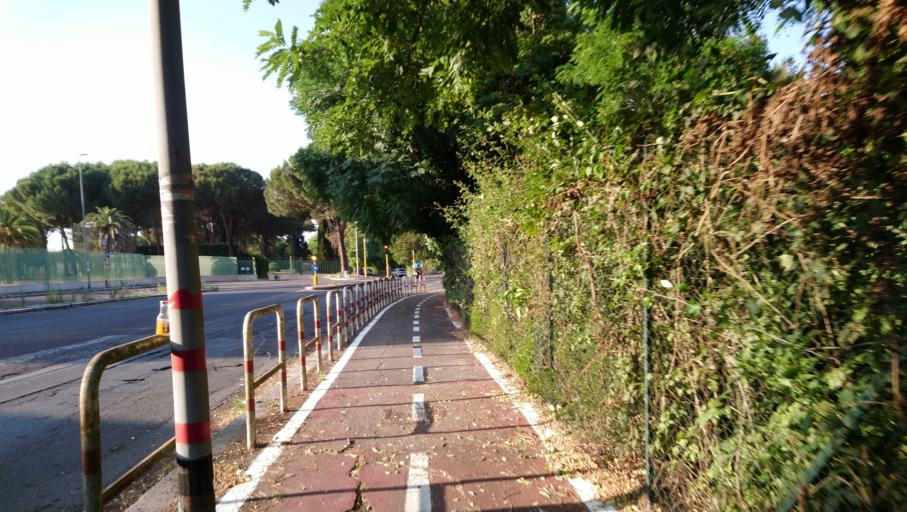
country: IT
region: Latium
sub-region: Citta metropolitana di Roma Capitale
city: Rome
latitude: 41.9350
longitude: 12.4960
